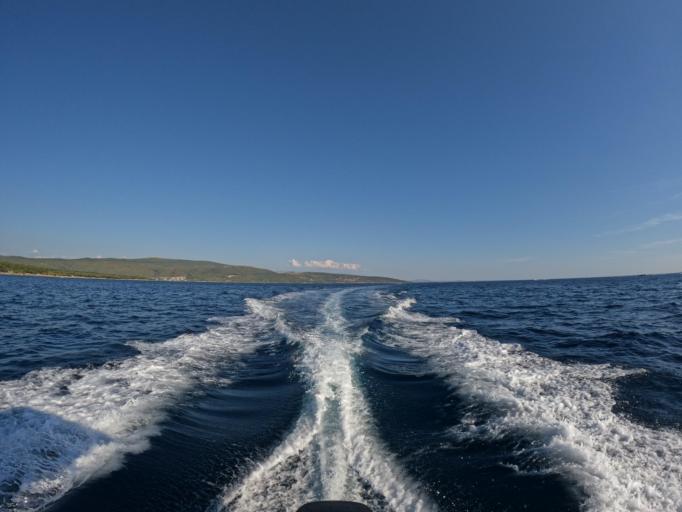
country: HR
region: Primorsko-Goranska
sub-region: Grad Krk
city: Krk
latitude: 45.0180
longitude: 14.5839
